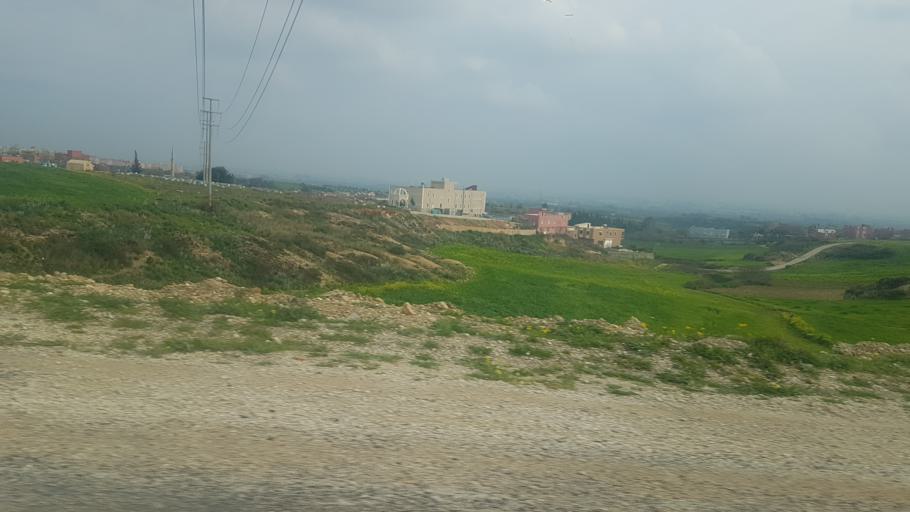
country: TR
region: Adana
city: Seyhan
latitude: 37.0463
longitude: 35.1934
